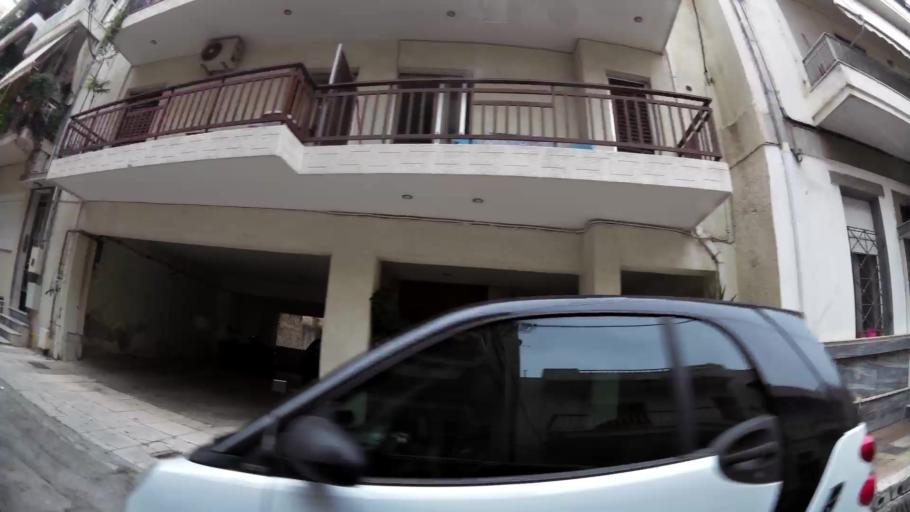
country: GR
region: Attica
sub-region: Nomos Attikis
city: Piraeus
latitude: 37.9313
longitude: 23.6394
